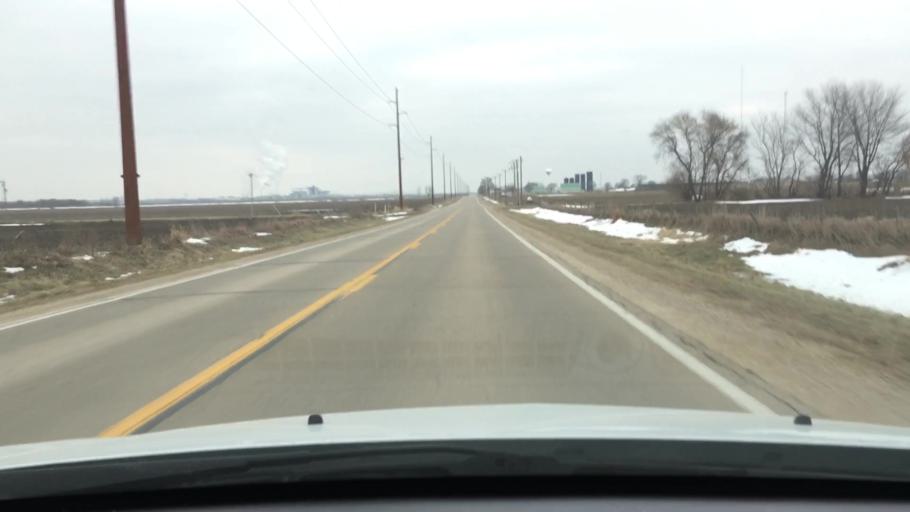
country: US
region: Illinois
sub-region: Ogle County
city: Rochelle
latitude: 41.8608
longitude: -89.0249
